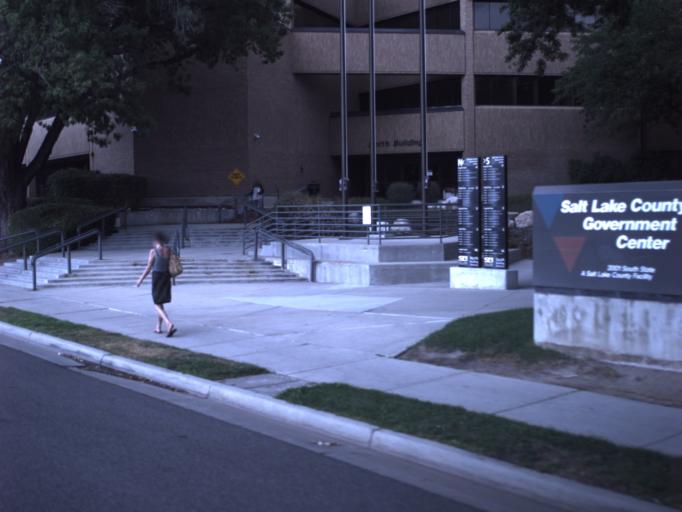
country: US
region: Utah
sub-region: Salt Lake County
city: South Salt Lake
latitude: 40.7272
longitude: -111.8881
